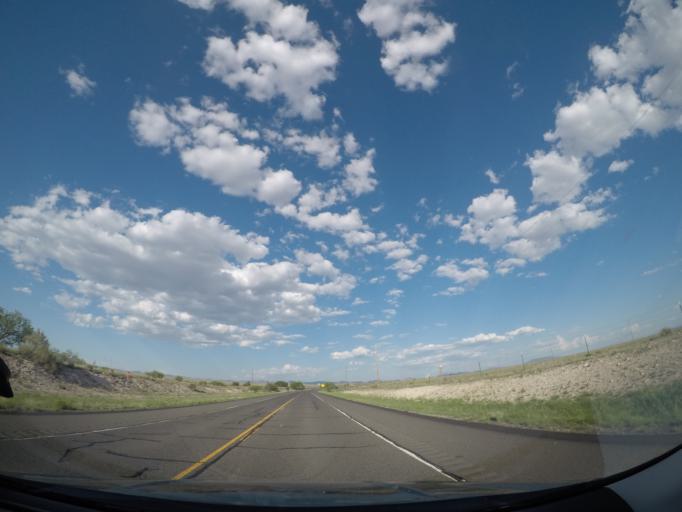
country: US
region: Texas
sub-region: Presidio County
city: Marfa
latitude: 30.2989
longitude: -103.9689
